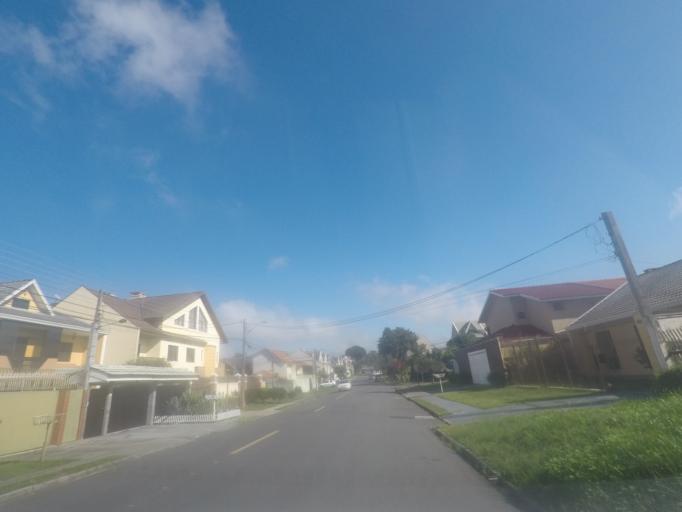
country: BR
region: Parana
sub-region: Pinhais
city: Pinhais
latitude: -25.4601
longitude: -49.2272
